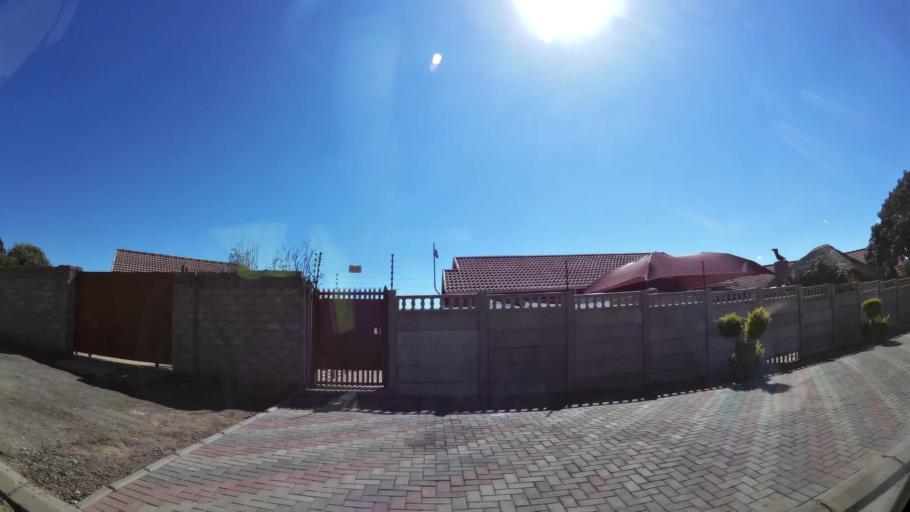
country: ZA
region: Limpopo
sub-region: Capricorn District Municipality
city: Polokwane
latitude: -23.8678
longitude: 29.4299
